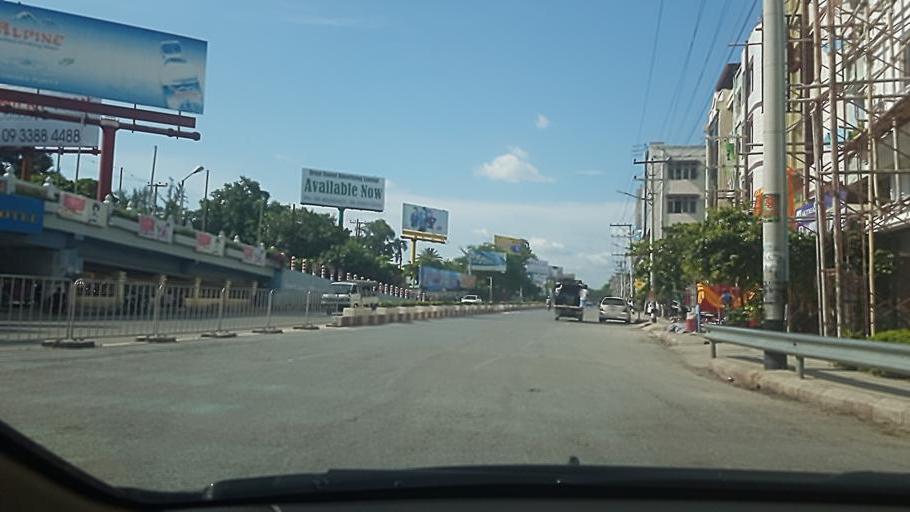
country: MM
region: Mandalay
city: Mandalay
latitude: 21.9770
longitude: 96.0871
